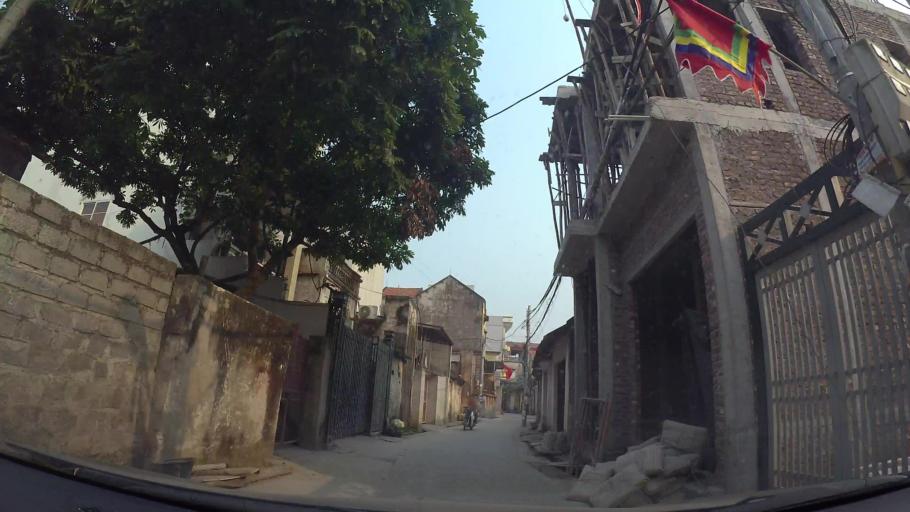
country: VN
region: Ha Noi
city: Thuong Tin
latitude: 20.8668
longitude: 105.8767
